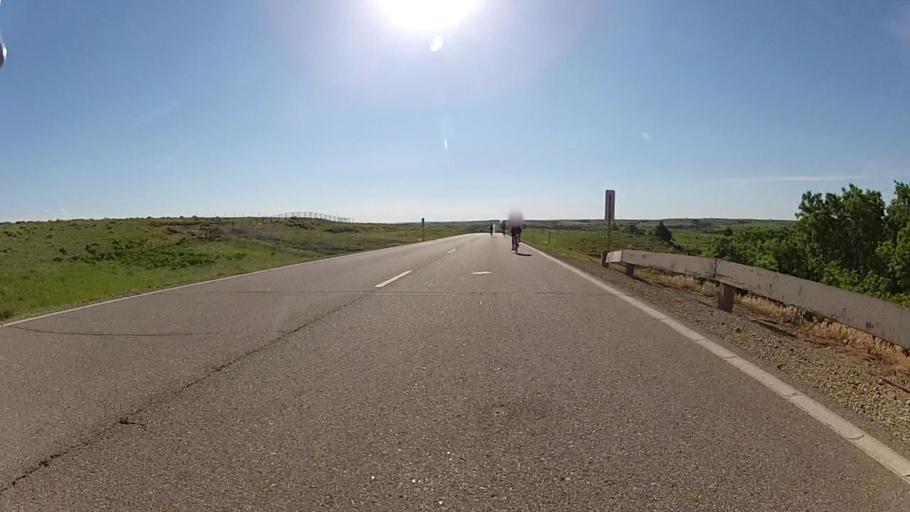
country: US
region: Kansas
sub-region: Barber County
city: Medicine Lodge
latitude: 37.2815
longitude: -98.8848
